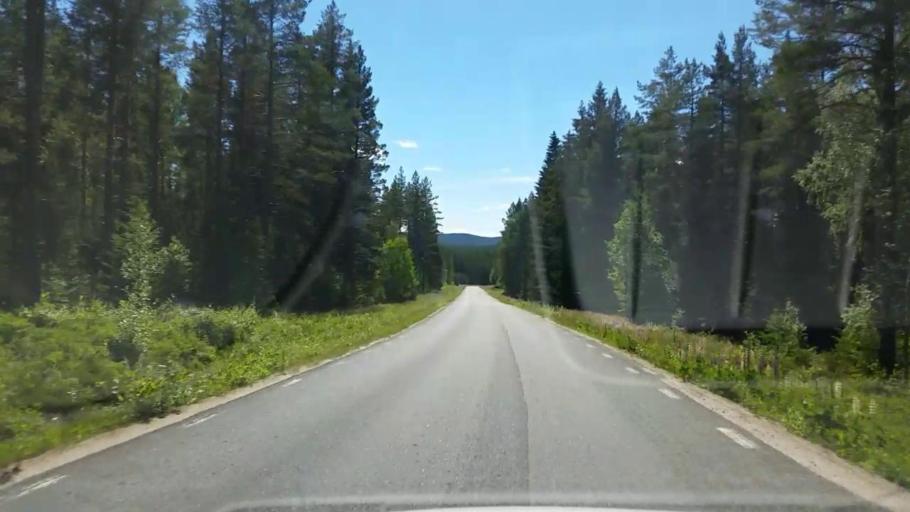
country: SE
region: Gaevleborg
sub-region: Ljusdals Kommun
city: Farila
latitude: 61.6725
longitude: 15.6164
